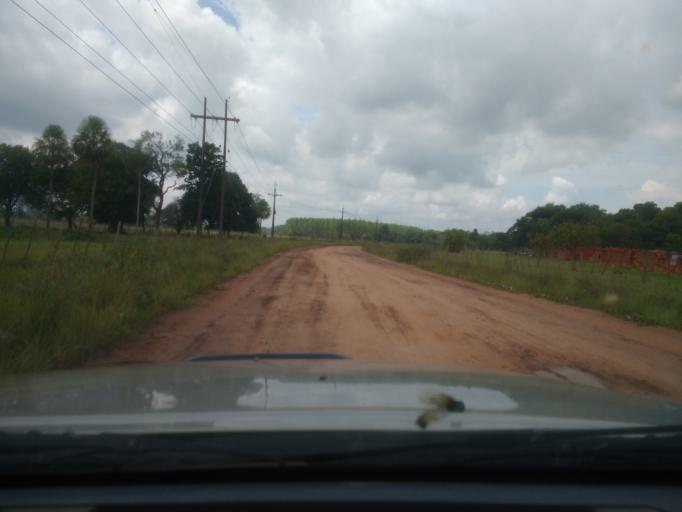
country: PY
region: San Pedro
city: Puerto Rosario
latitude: -24.3934
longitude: -57.1044
